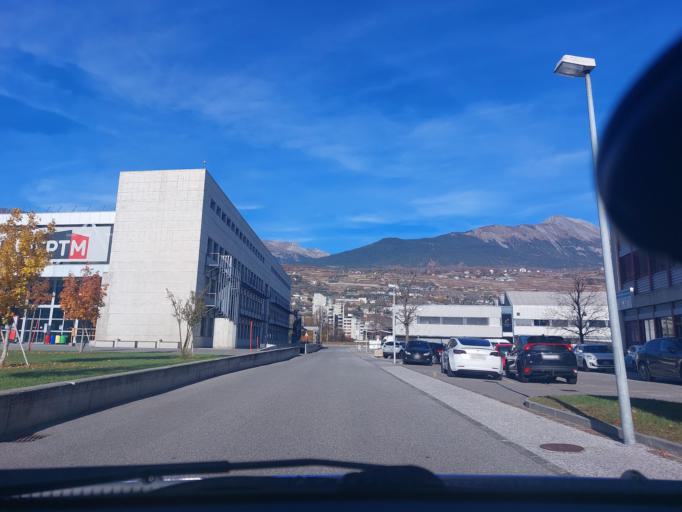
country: CH
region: Valais
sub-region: Sion District
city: Sitten
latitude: 46.2244
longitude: 7.3513
